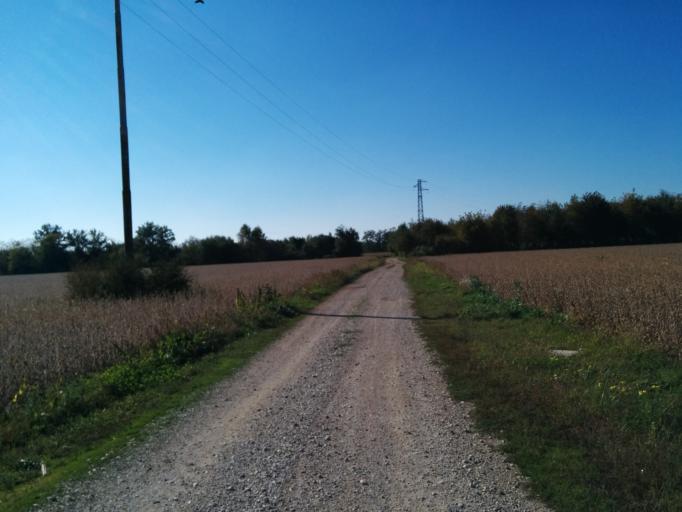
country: IT
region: Friuli Venezia Giulia
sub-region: Provincia di Udine
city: Colugna
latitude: 46.0917
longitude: 13.1811
